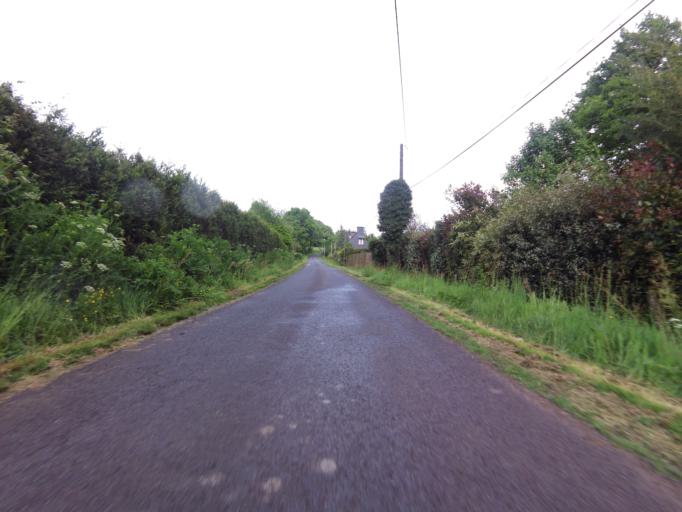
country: FR
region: Brittany
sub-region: Departement du Morbihan
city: Pluherlin
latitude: 47.7125
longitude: -2.3673
